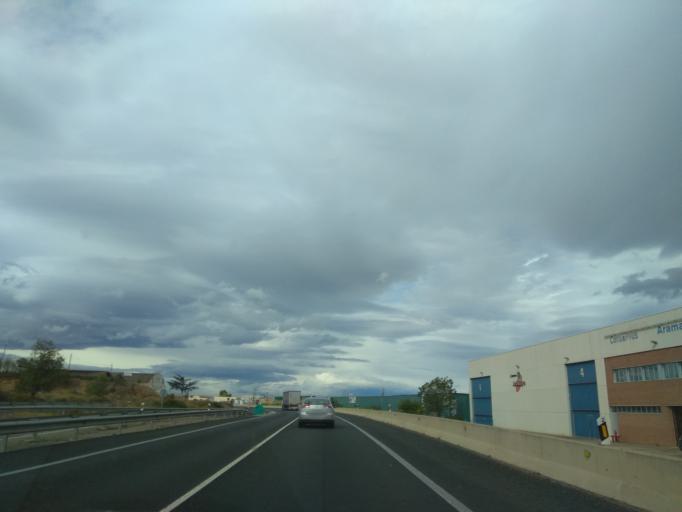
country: ES
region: La Rioja
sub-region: Provincia de La Rioja
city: Rincon de Soto
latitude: 42.2252
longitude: -1.8416
